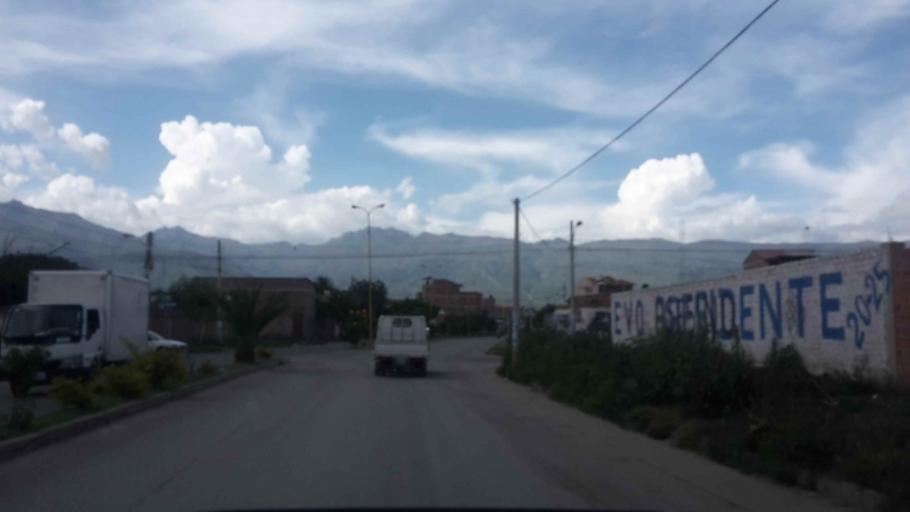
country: BO
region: Cochabamba
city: Cochabamba
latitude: -17.4004
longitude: -66.2737
